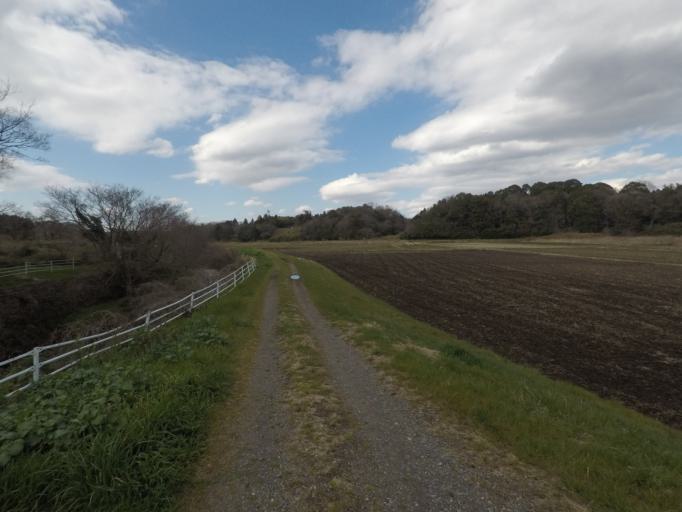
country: JP
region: Ibaraki
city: Ushiku
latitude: 35.9959
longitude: 140.1168
